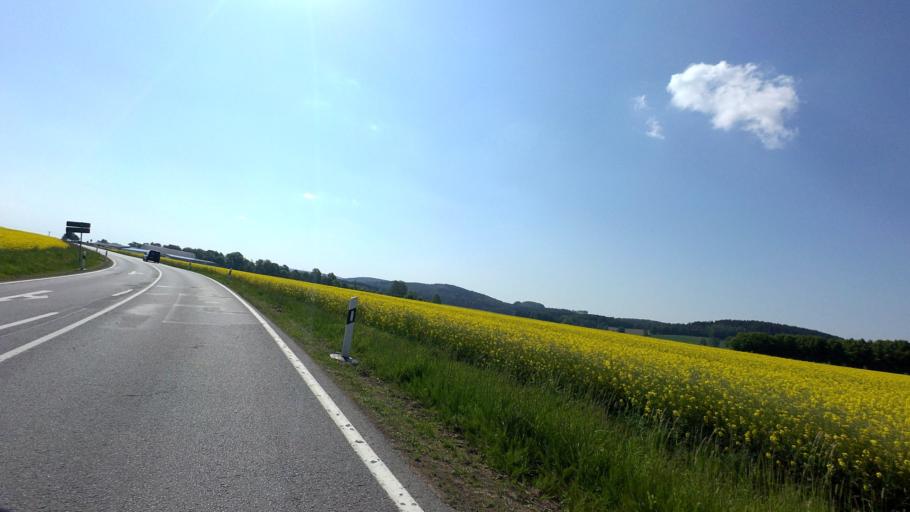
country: DE
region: Saxony
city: Stolpen
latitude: 51.0374
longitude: 14.1373
